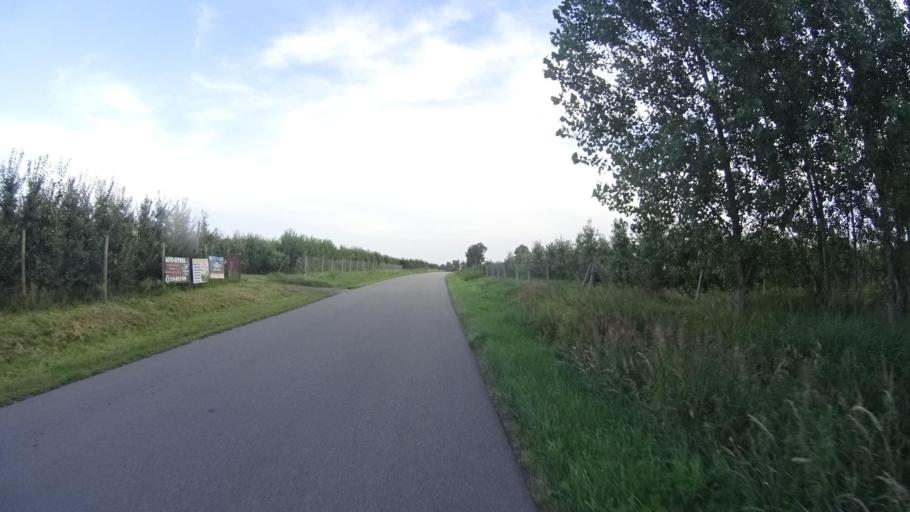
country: PL
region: Masovian Voivodeship
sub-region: Powiat grojecki
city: Goszczyn
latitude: 51.7039
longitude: 20.8547
